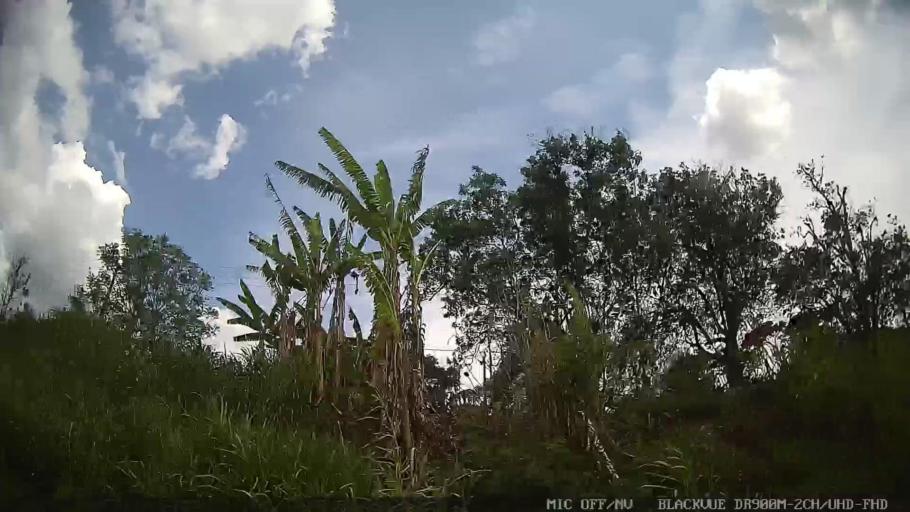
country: BR
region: Sao Paulo
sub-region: Itatiba
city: Itatiba
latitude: -22.9607
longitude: -46.7105
